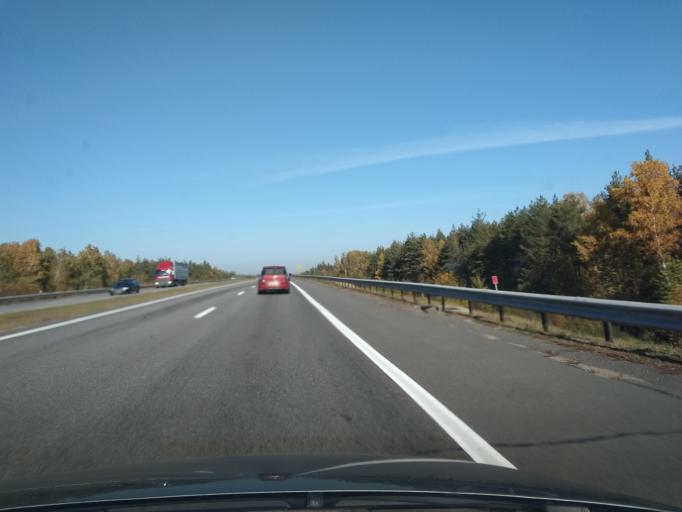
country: BY
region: Grodnenskaya
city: Zhyrovichy
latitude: 52.9098
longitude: 25.6807
